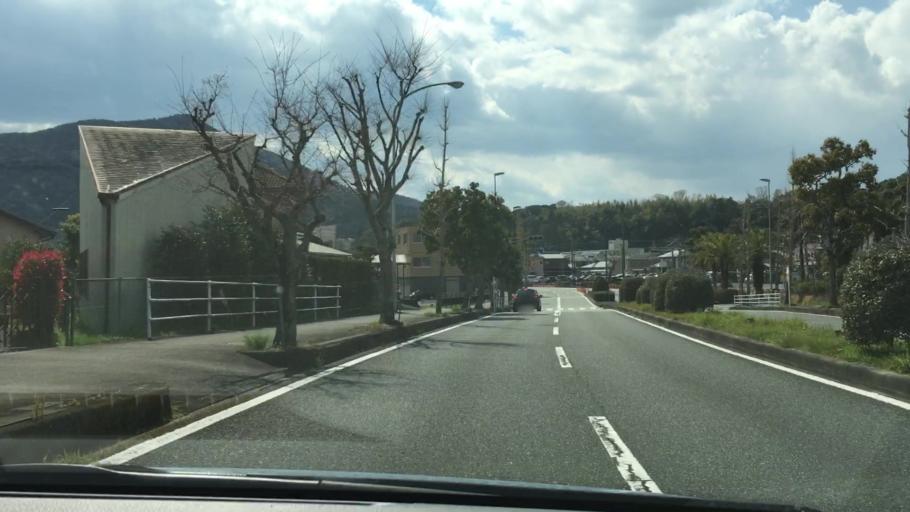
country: JP
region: Mie
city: Ise
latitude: 34.4700
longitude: 136.7267
